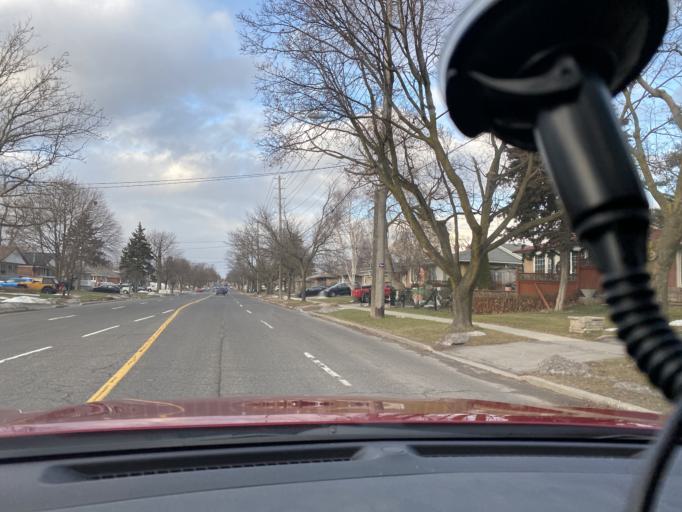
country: CA
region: Ontario
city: Scarborough
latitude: 43.7702
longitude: -79.2188
